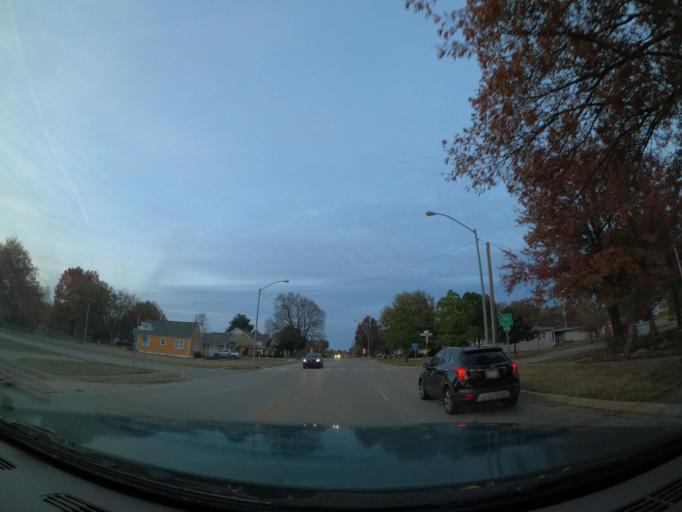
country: US
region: Oklahoma
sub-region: Tulsa County
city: Broken Arrow
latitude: 36.0578
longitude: -95.7908
